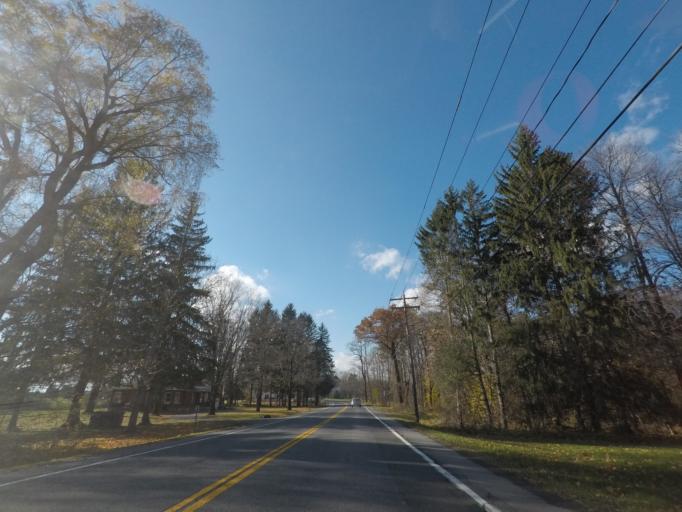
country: US
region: New York
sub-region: Saratoga County
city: Country Knolls
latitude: 42.8933
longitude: -73.8482
